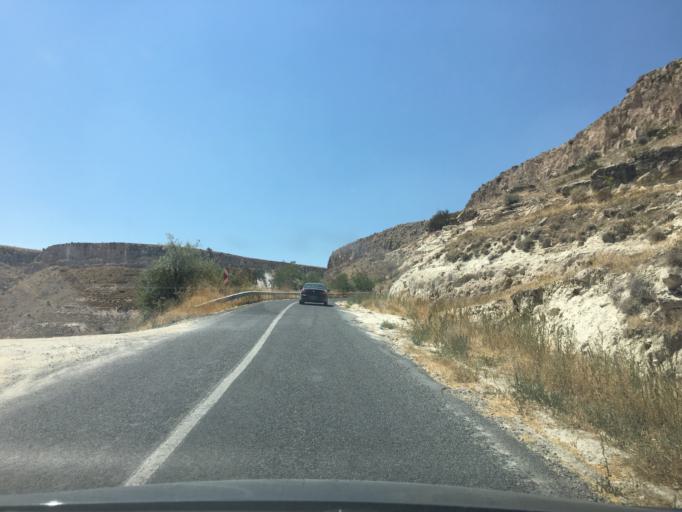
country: TR
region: Nevsehir
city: Urgub
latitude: 38.4689
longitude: 34.9406
